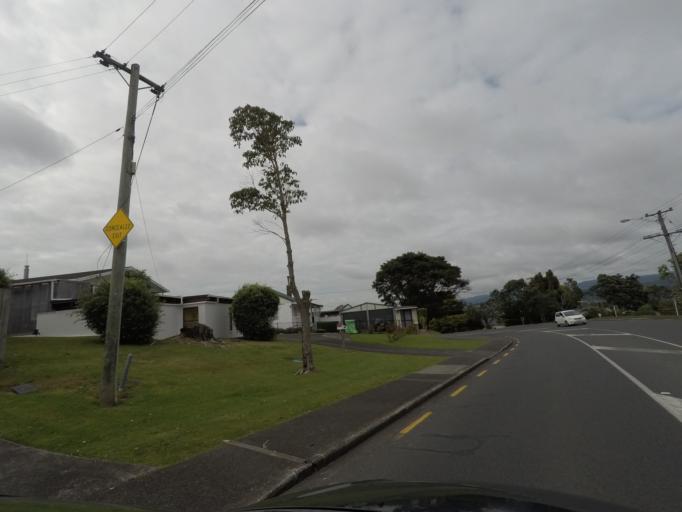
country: NZ
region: Auckland
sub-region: Auckland
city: Rosebank
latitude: -36.8465
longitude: 174.6080
